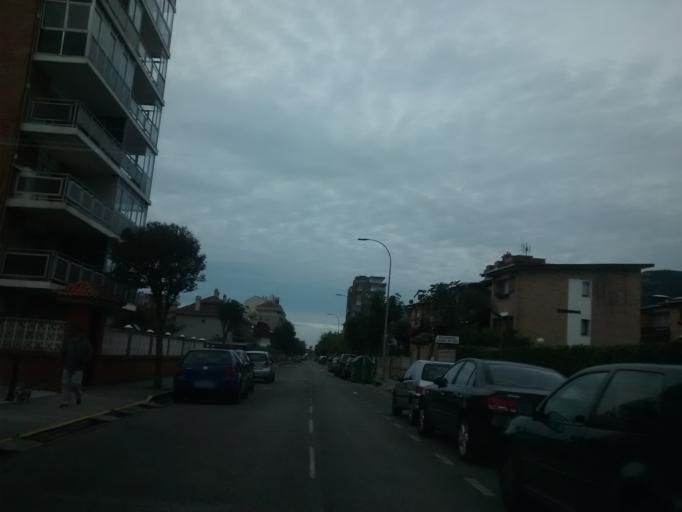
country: ES
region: Cantabria
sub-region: Provincia de Cantabria
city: Santona
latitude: 43.4256
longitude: -3.4472
